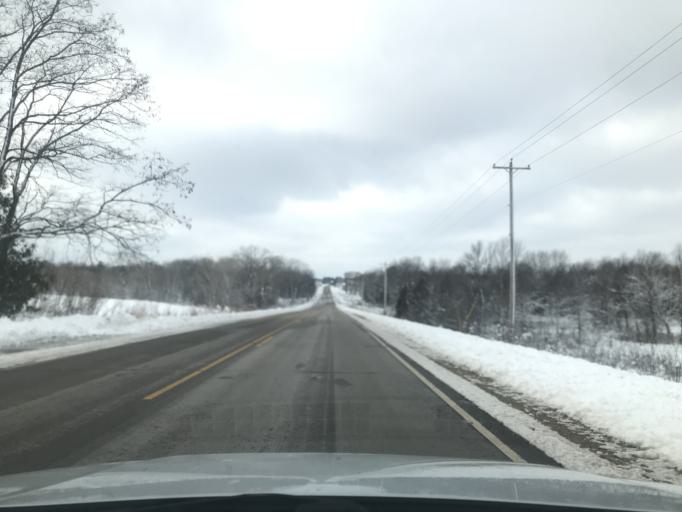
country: US
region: Wisconsin
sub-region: Oconto County
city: Oconto
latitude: 44.9500
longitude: -87.9531
